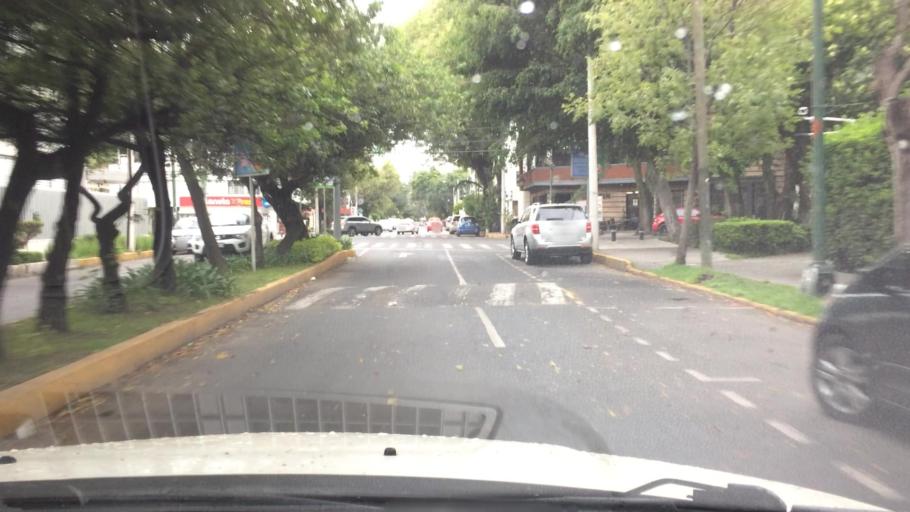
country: MX
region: Mexico City
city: Alvaro Obregon
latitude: 19.3646
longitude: -99.1849
